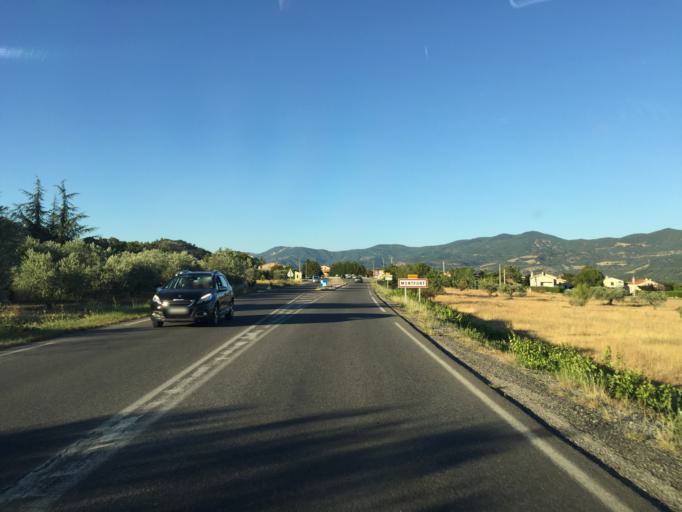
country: FR
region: Provence-Alpes-Cote d'Azur
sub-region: Departement des Alpes-de-Haute-Provence
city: Les Mees
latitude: 44.0614
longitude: 5.9756
